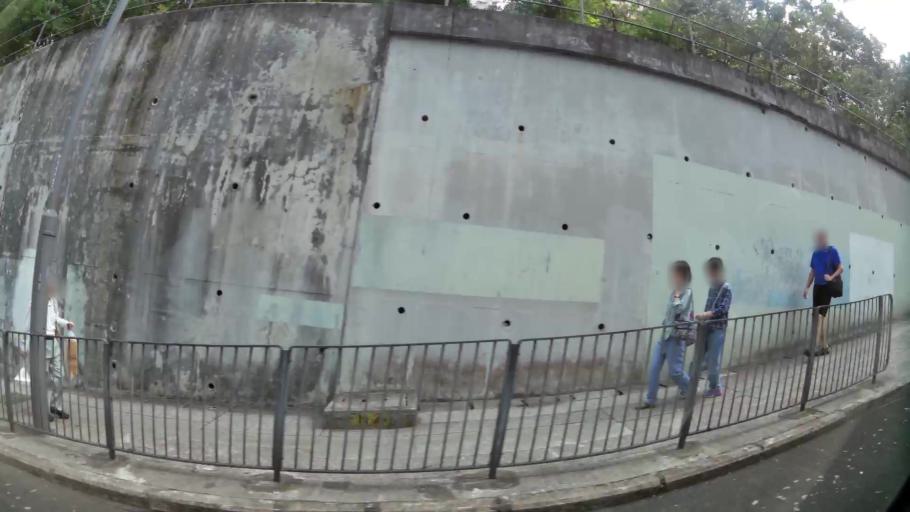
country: HK
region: Wanchai
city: Wan Chai
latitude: 22.2874
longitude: 114.1955
